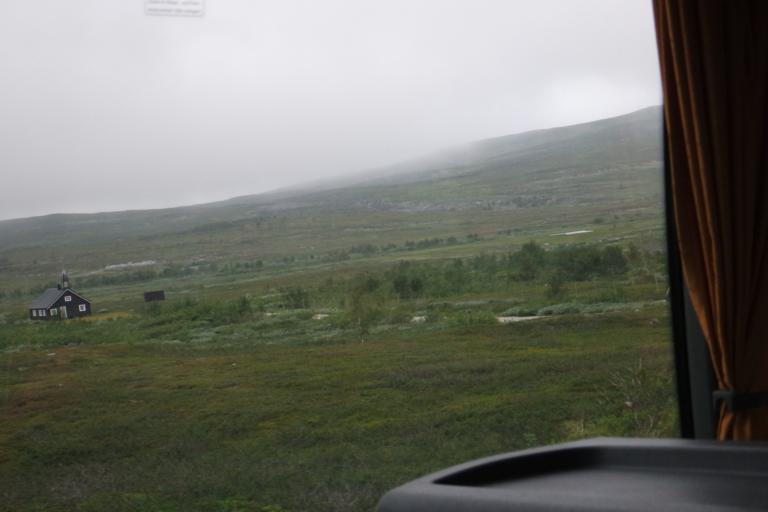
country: NO
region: Finnmark Fylke
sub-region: Kvalsund
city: Kvalsund
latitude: 70.2712
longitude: 24.1017
